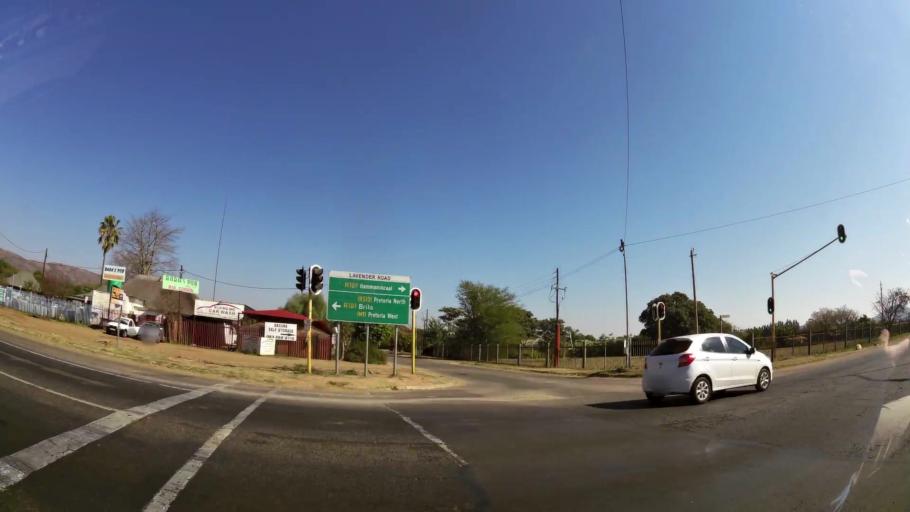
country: ZA
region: Gauteng
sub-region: City of Tshwane Metropolitan Municipality
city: Pretoria
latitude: -25.6689
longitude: 28.1933
